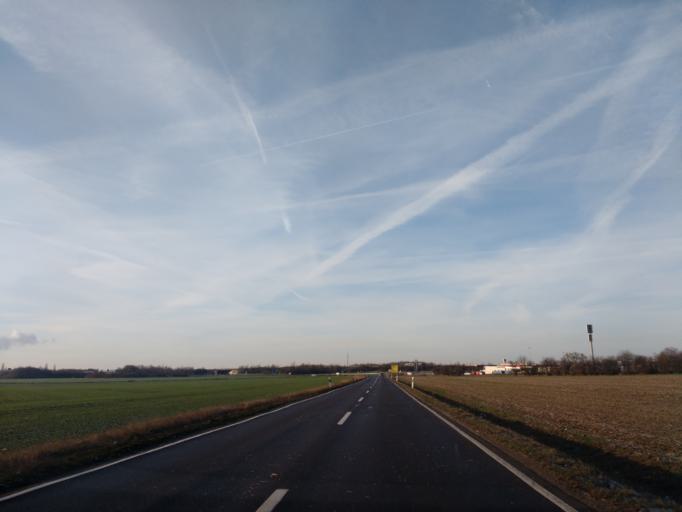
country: DE
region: Saxony-Anhalt
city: Oppin
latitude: 51.5463
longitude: 12.0192
